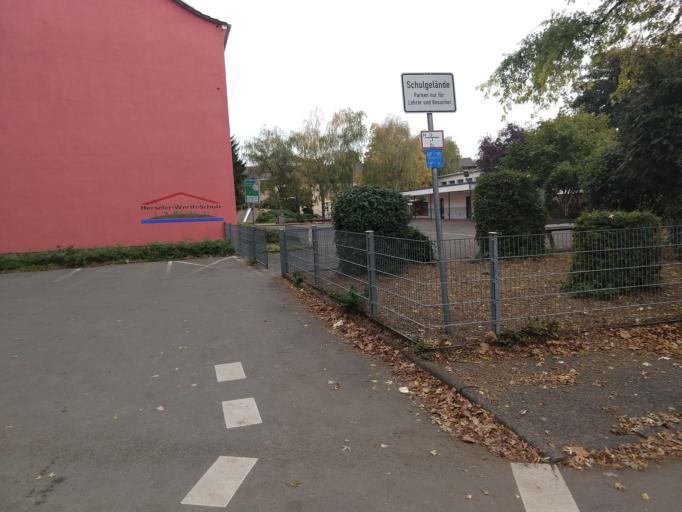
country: DE
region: North Rhine-Westphalia
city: Niederkassel
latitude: 50.7725
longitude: 7.0473
